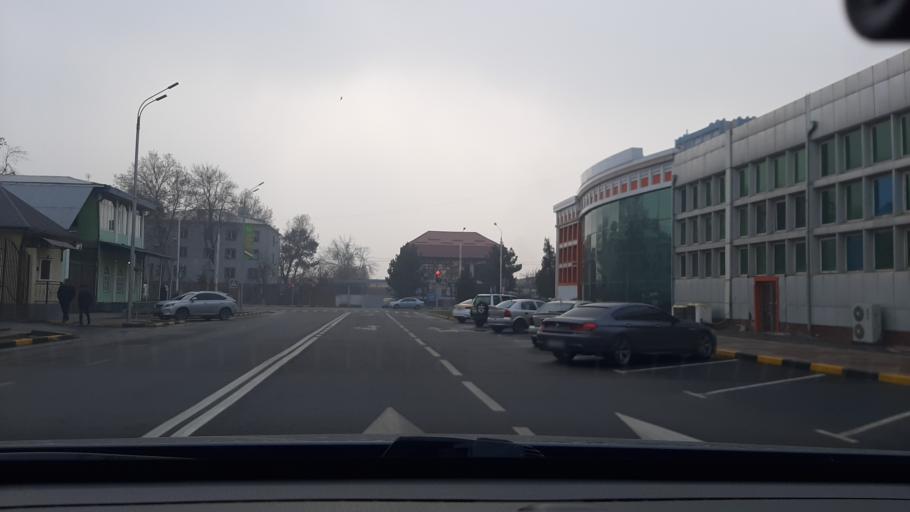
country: TJ
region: Dushanbe
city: Dushanbe
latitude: 38.5586
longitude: 68.7953
